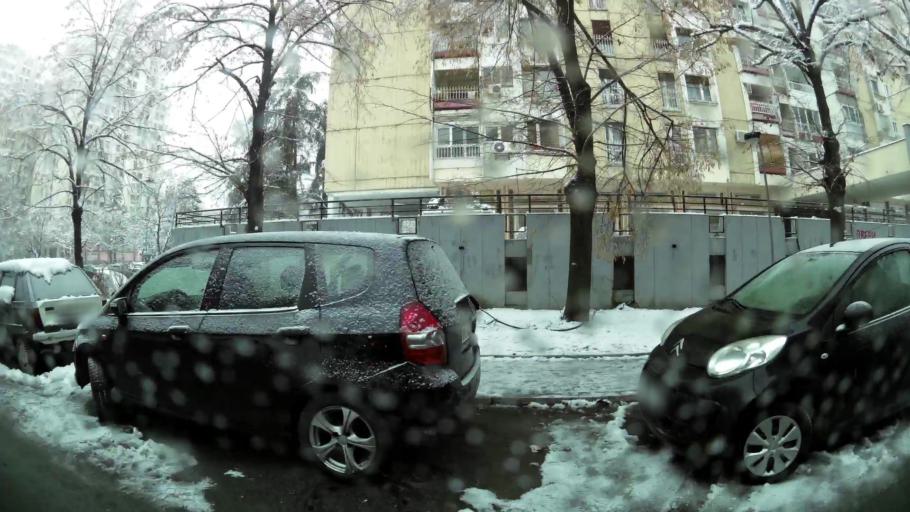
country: RS
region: Central Serbia
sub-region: Belgrade
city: Novi Beograd
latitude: 44.8200
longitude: 20.4199
